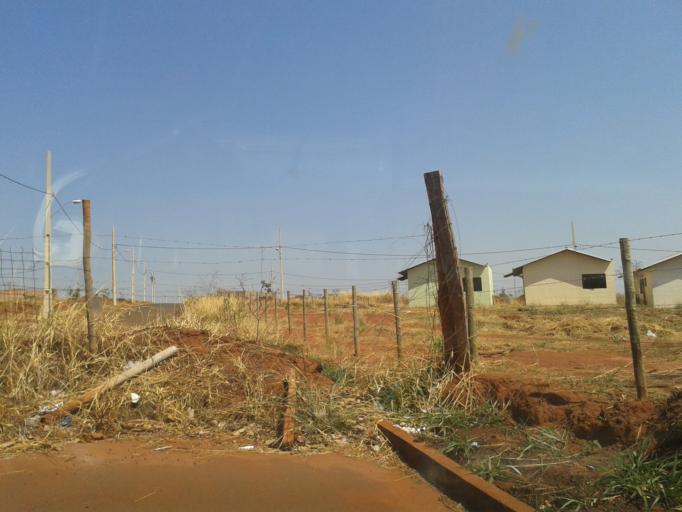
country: BR
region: Minas Gerais
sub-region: Ituiutaba
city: Ituiutaba
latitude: -19.0149
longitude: -49.4555
